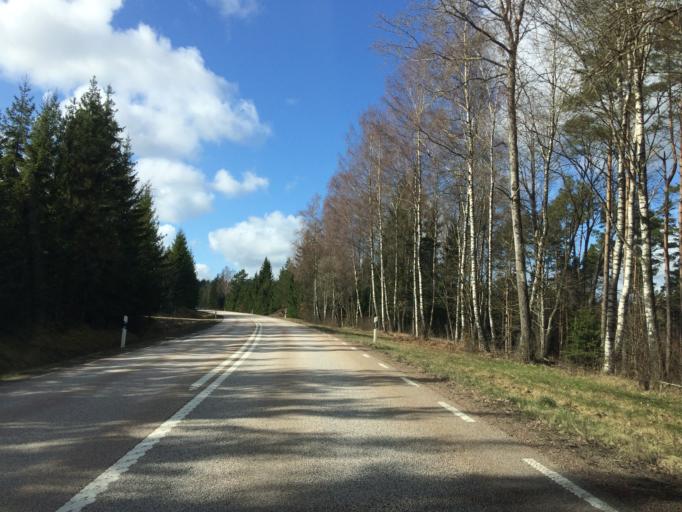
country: SE
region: Kronoberg
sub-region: Markaryds Kommun
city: Markaryd
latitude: 56.4763
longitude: 13.5115
